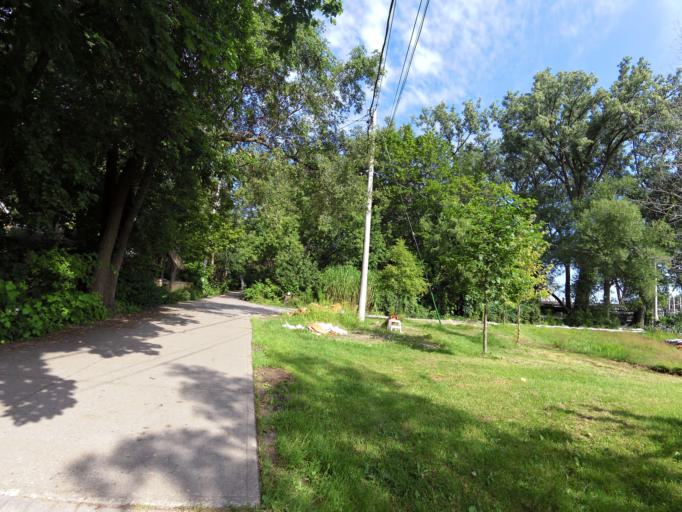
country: CA
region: Ontario
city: Toronto
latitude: 43.6286
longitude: -79.3576
